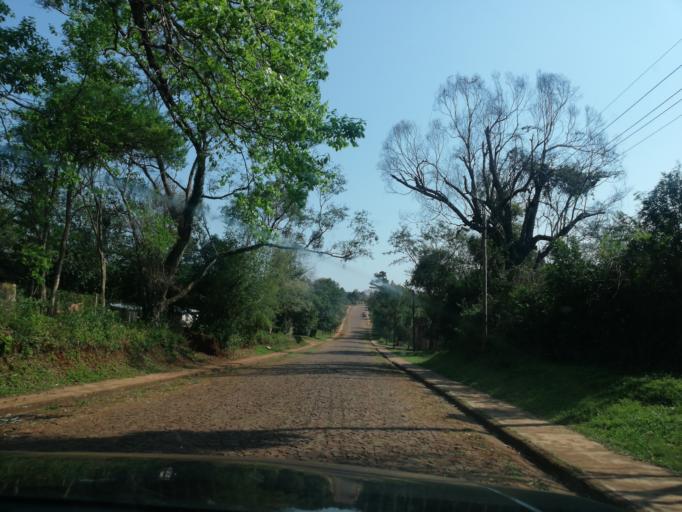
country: AR
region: Misiones
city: Bonpland
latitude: -27.4836
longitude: -55.4806
